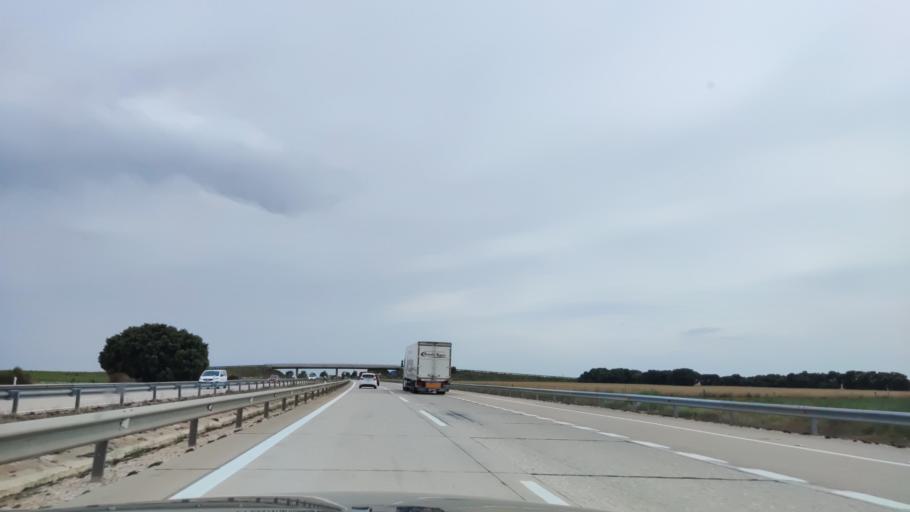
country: ES
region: Castille-La Mancha
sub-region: Provincia de Cuenca
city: Pozoamargo
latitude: 39.3182
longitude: -2.2037
